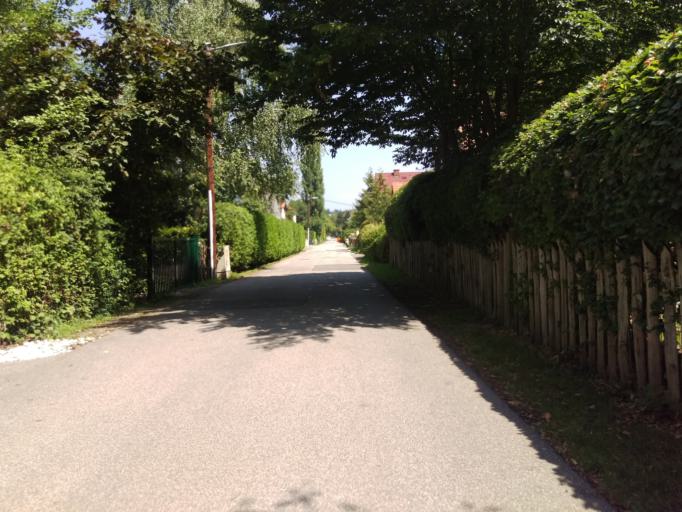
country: AT
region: Styria
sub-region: Graz Stadt
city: Graz
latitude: 47.0502
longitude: 15.4716
